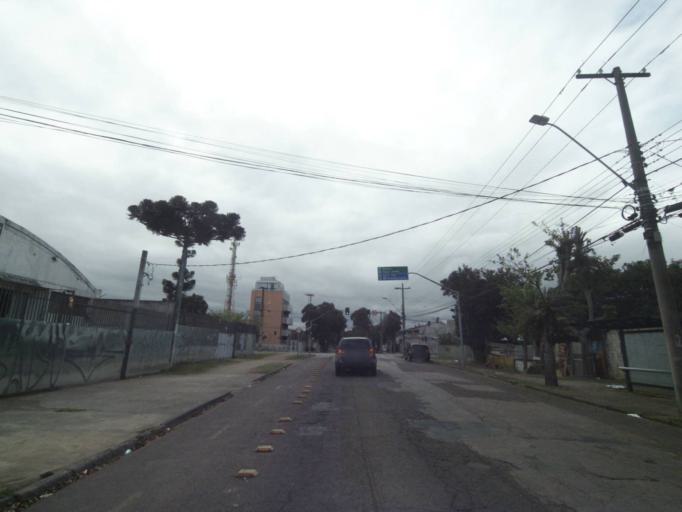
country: BR
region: Parana
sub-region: Curitiba
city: Curitiba
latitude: -25.4466
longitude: -49.2539
